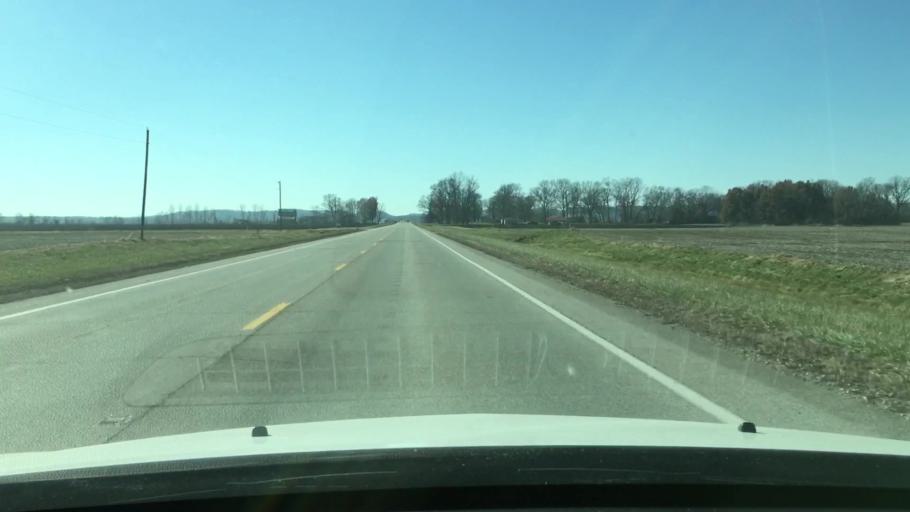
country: US
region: Missouri
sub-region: Pike County
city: Louisiana
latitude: 39.4931
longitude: -91.0060
